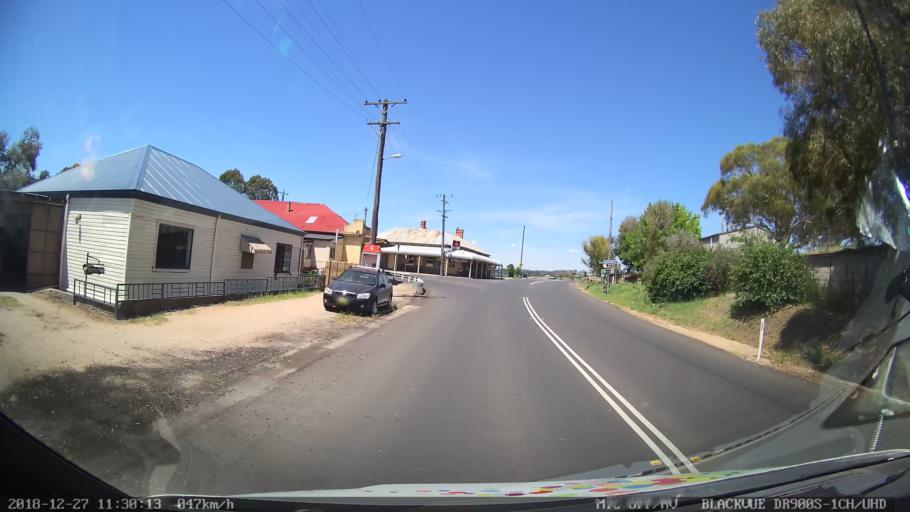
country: AU
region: New South Wales
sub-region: Bathurst Regional
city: Perthville
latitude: -33.4863
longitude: 149.5470
